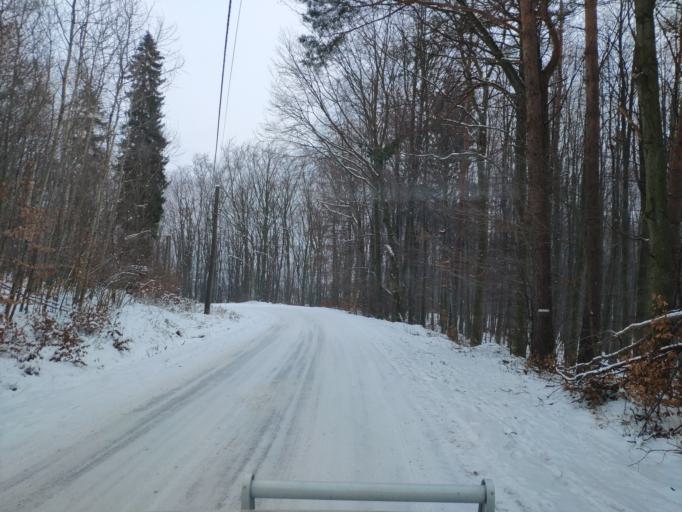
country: SK
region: Kosicky
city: Medzev
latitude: 48.7539
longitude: 21.0003
